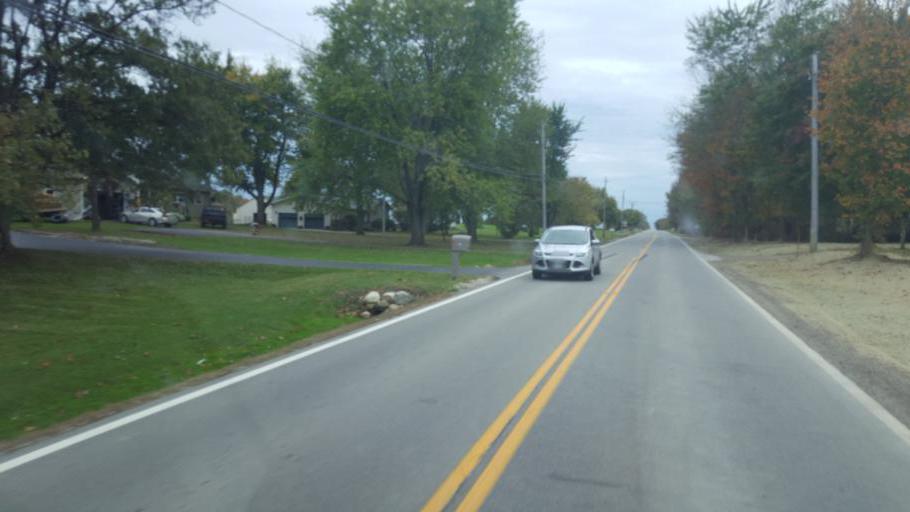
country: US
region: Ohio
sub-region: Huron County
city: Wakeman
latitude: 41.2925
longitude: -82.3760
